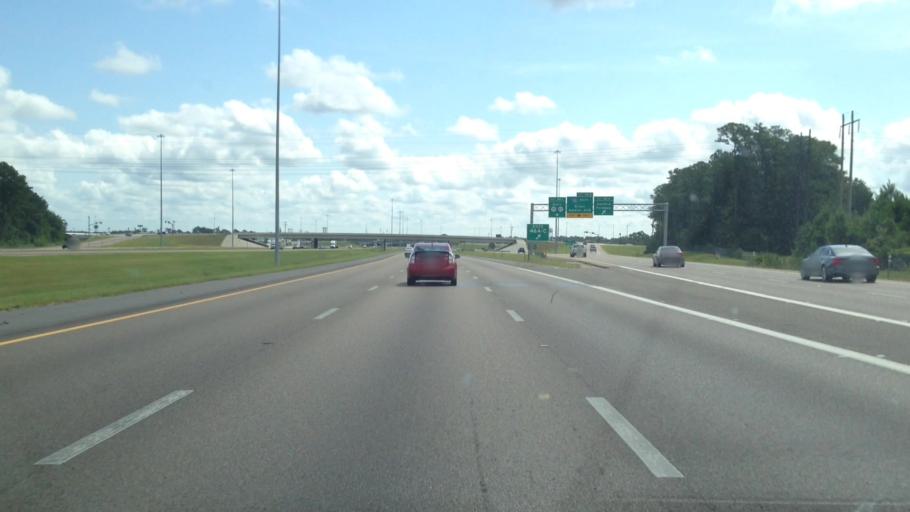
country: US
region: Mississippi
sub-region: Harrison County
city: D'Iberville
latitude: 30.4488
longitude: -88.9089
